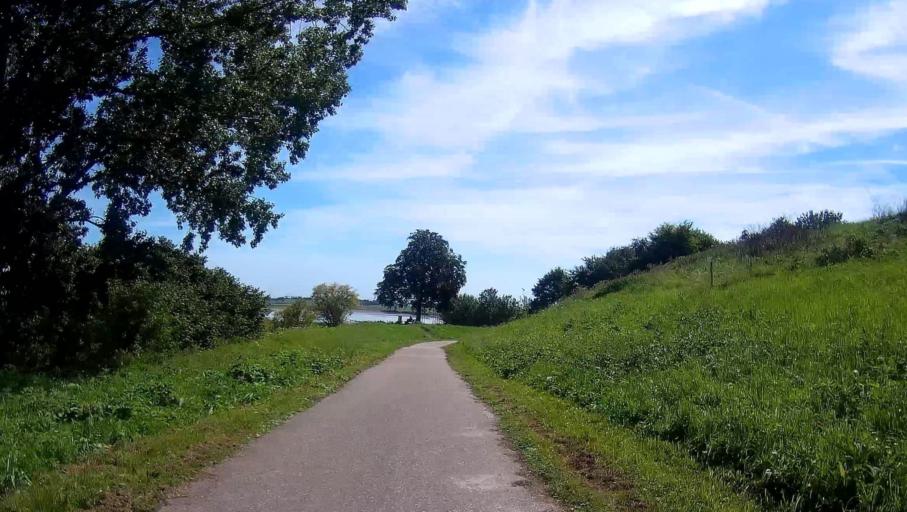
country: NL
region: South Holland
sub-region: Gemeente Hendrik-Ido-Ambacht
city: Hendrik-Ido-Ambacht
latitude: 51.8680
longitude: 4.6300
